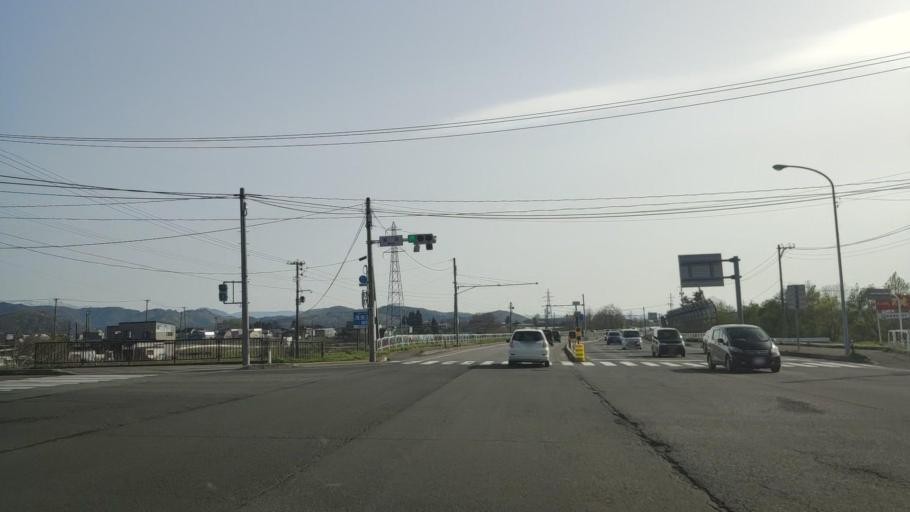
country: JP
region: Aomori
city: Aomori Shi
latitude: 40.8464
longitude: 140.8358
